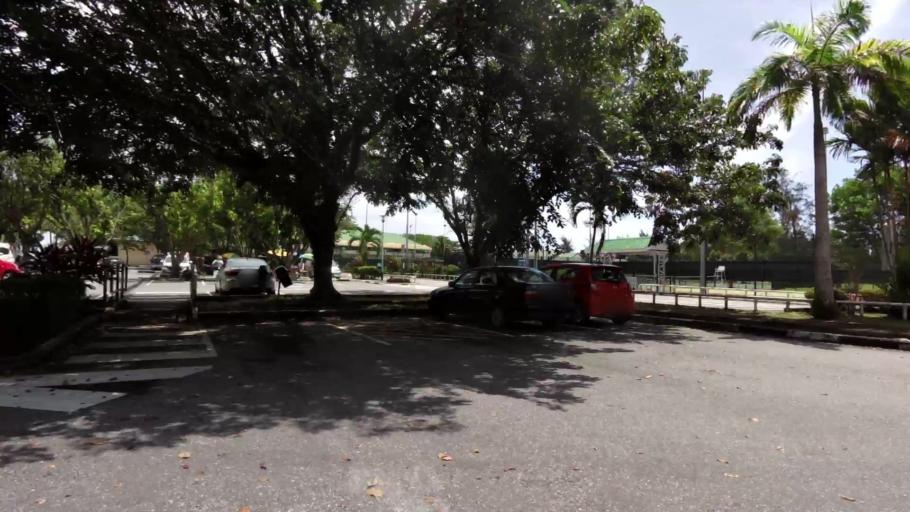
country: BN
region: Belait
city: Kuala Belait
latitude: 4.6004
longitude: 114.2702
